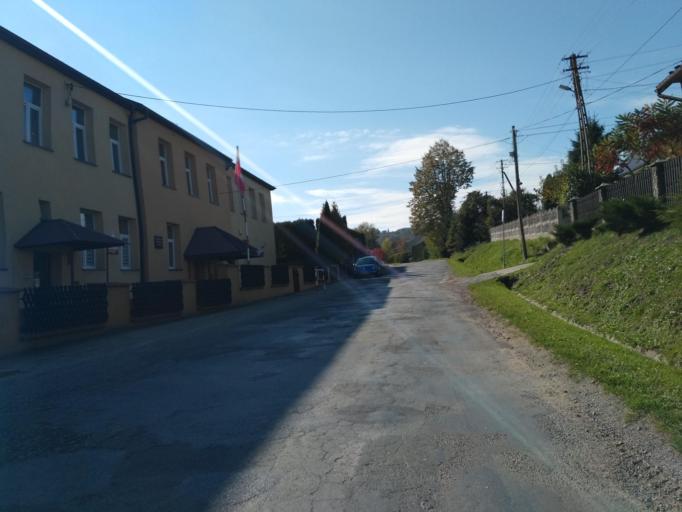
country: PL
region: Subcarpathian Voivodeship
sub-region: Powiat debicki
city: Slotowa
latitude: 49.9436
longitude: 21.2867
